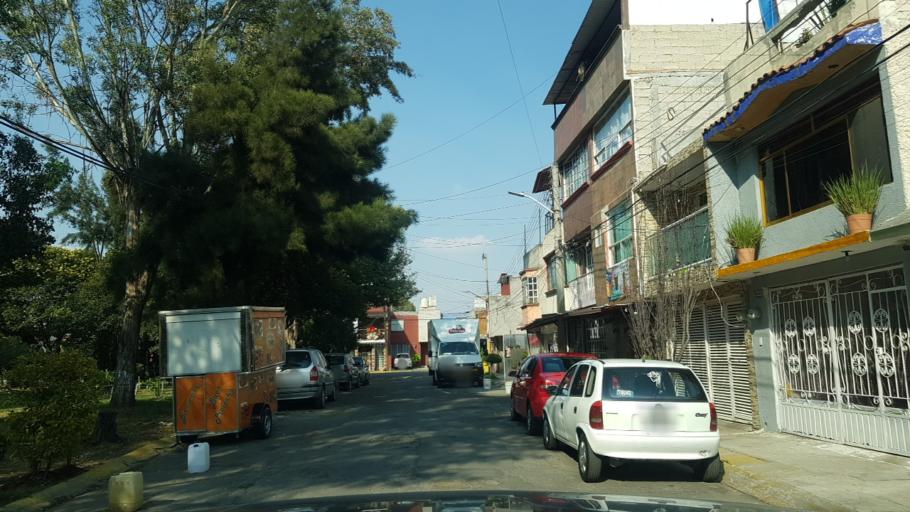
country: MX
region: Mexico
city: Santiago Teyahualco
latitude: 19.6529
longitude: -99.1164
